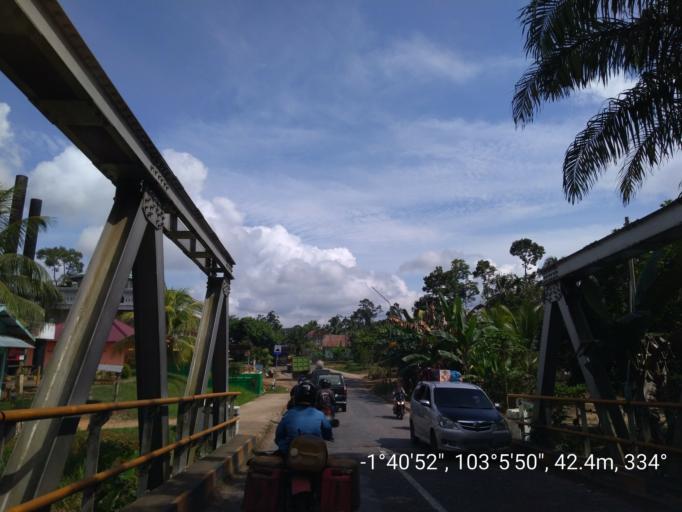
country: ID
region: Jambi
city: Muara Tembesi
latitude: -1.6822
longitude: 103.0989
